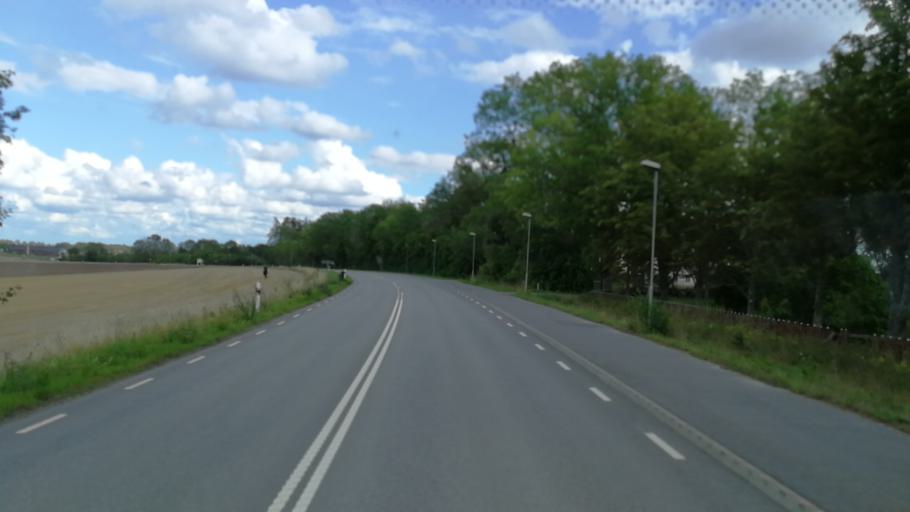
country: SE
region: OEstergoetland
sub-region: Linkopings Kommun
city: Ljungsbro
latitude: 58.4913
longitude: 15.4726
